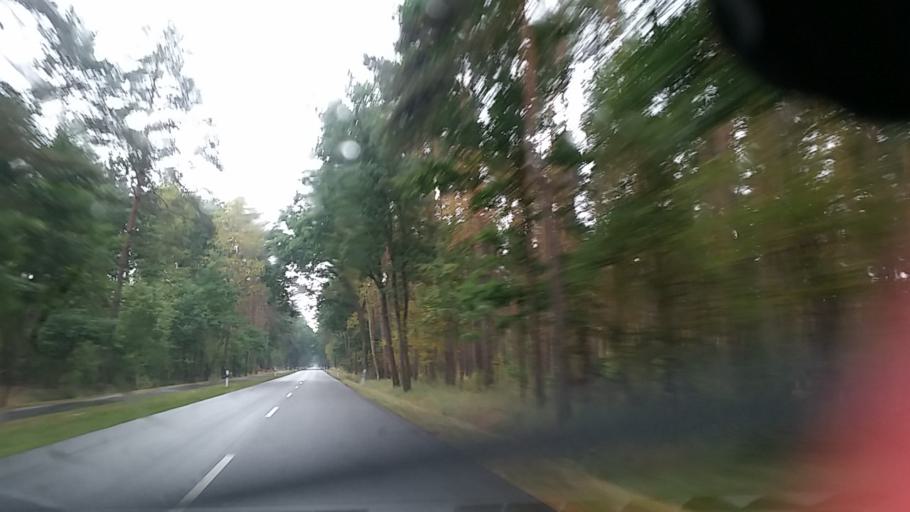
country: DE
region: Lower Saxony
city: Bokensdorf
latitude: 52.5210
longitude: 10.7162
